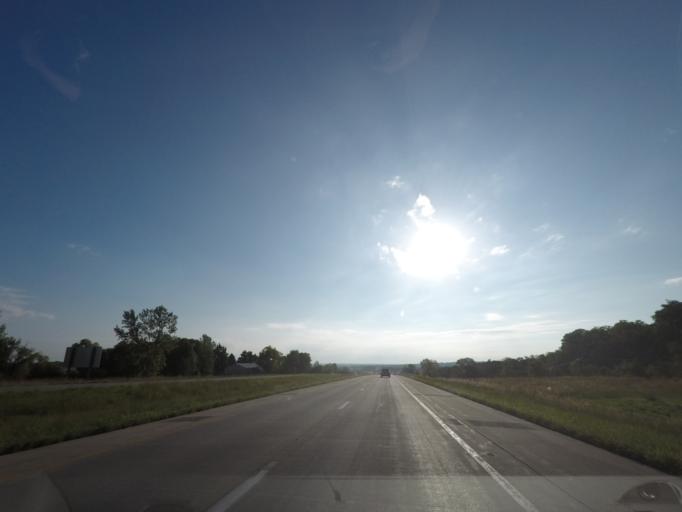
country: US
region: Iowa
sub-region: Warren County
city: Carlisle
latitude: 41.5116
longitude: -93.5423
